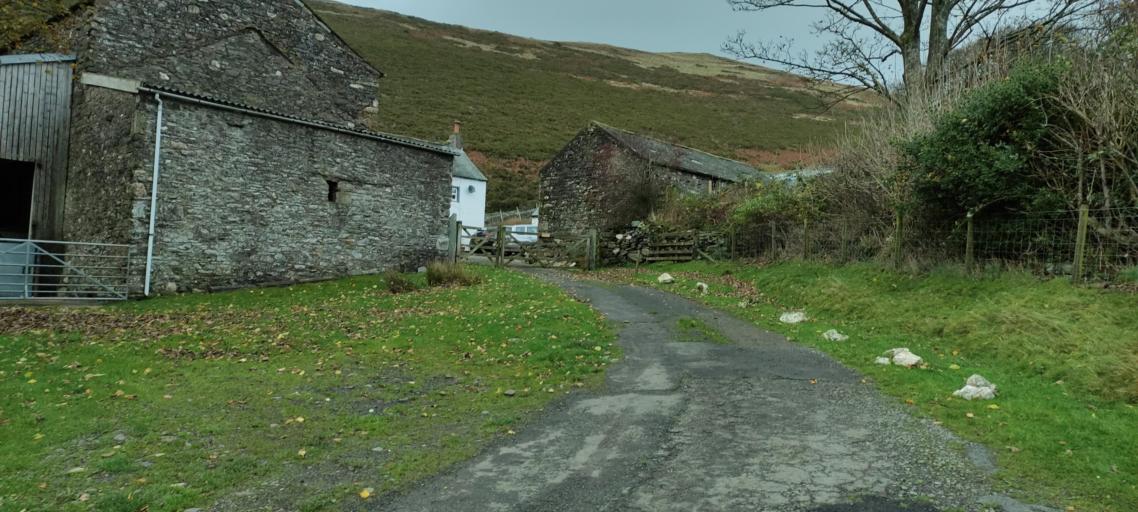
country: GB
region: England
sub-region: Cumbria
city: Cockermouth
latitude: 54.6515
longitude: -3.2539
